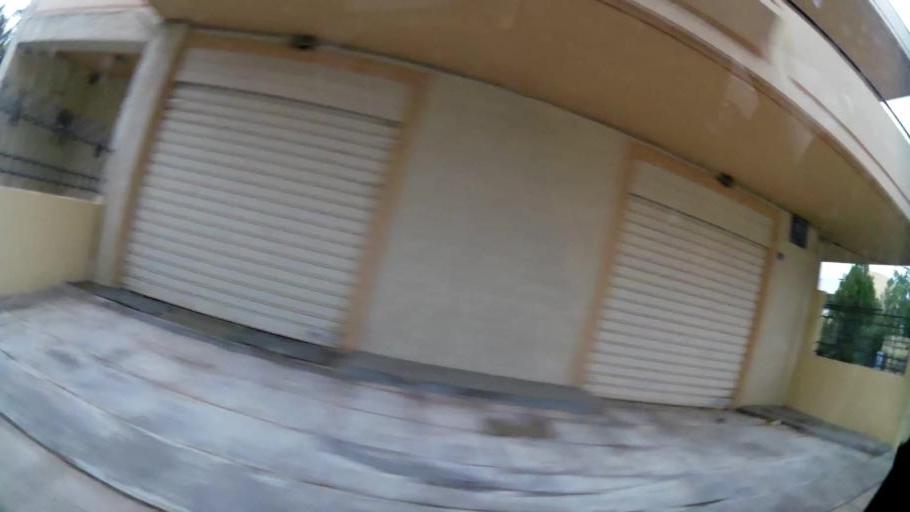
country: GR
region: Attica
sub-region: Nomarchia Athinas
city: Agioi Anargyroi
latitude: 38.0384
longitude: 23.7258
